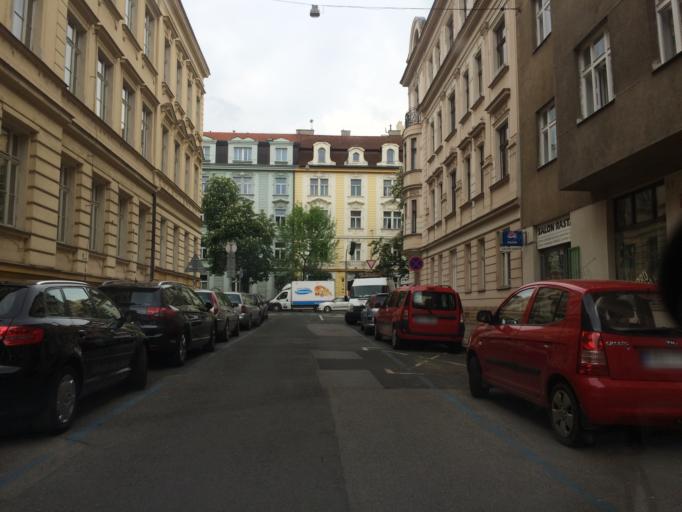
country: CZ
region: Praha
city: Prague
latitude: 50.1012
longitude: 14.4198
